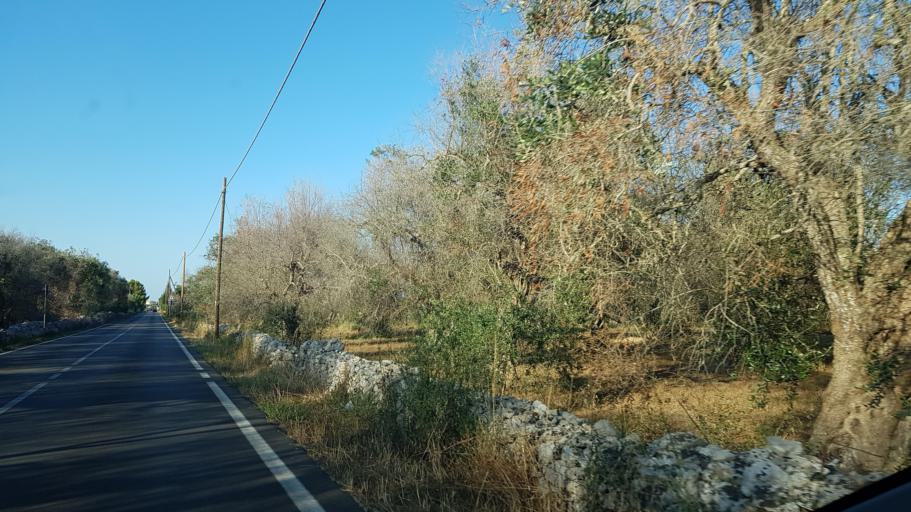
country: IT
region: Apulia
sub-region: Provincia di Lecce
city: Andrano
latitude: 39.9937
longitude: 18.3885
